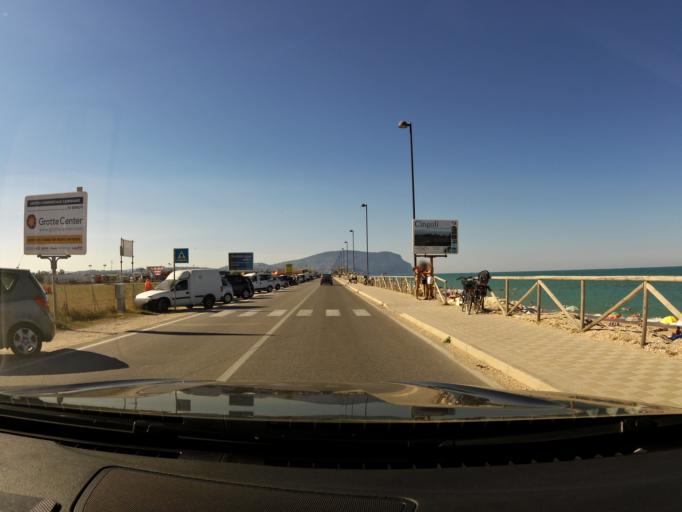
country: IT
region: The Marches
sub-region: Provincia di Macerata
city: Porto Recanati
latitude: 43.4576
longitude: 13.6507
